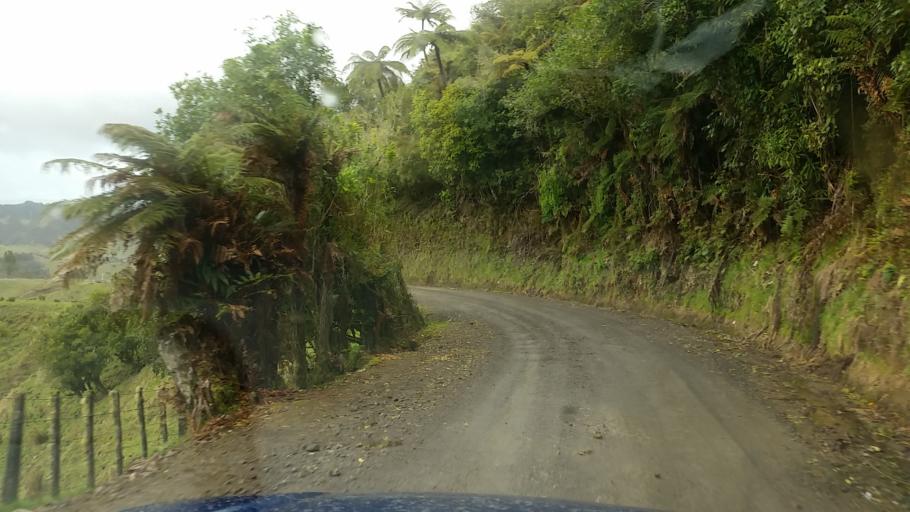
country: NZ
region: Taranaki
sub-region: South Taranaki District
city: Eltham
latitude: -39.1689
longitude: 174.6280
